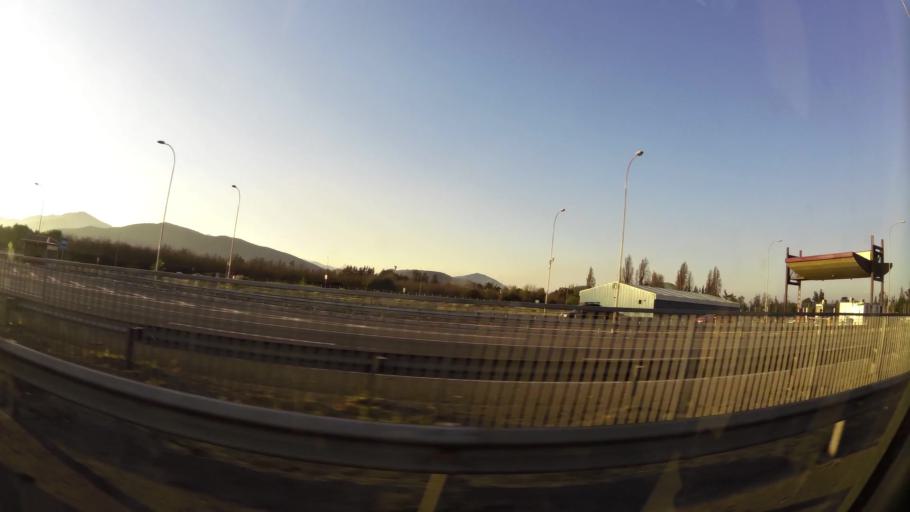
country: CL
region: Santiago Metropolitan
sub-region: Provincia de Talagante
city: Penaflor
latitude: -33.5590
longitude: -70.8292
